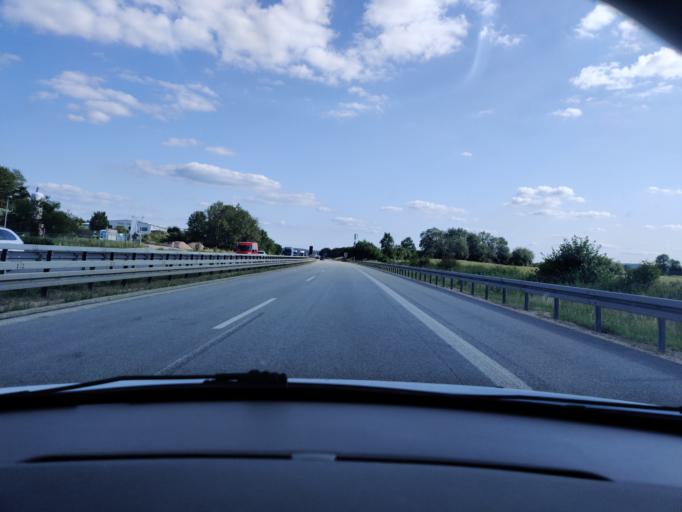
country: DE
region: Bavaria
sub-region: Upper Palatinate
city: Pfreimd
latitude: 49.4828
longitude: 12.1890
